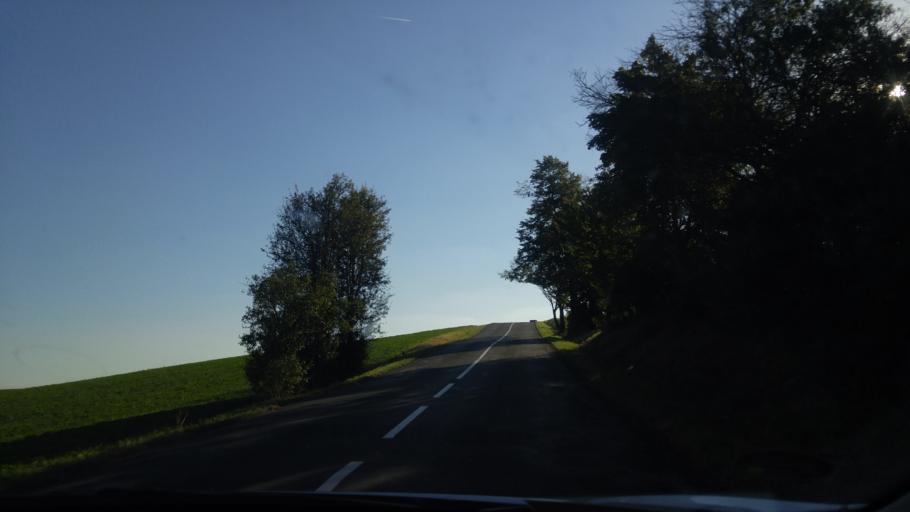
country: CZ
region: South Moravian
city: Veverska Bityska
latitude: 49.2361
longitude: 16.4354
